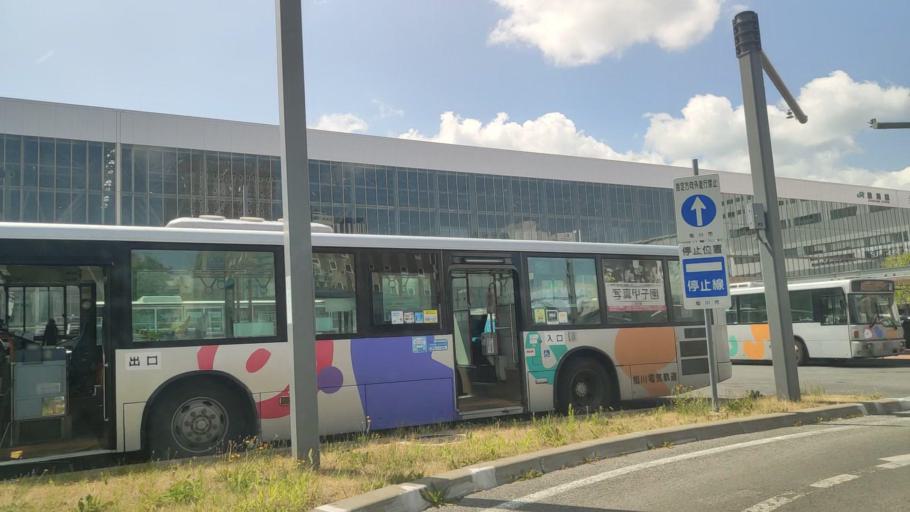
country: JP
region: Hokkaido
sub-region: Asahikawa-shi
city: Asahikawa
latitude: 43.7633
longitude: 142.3597
